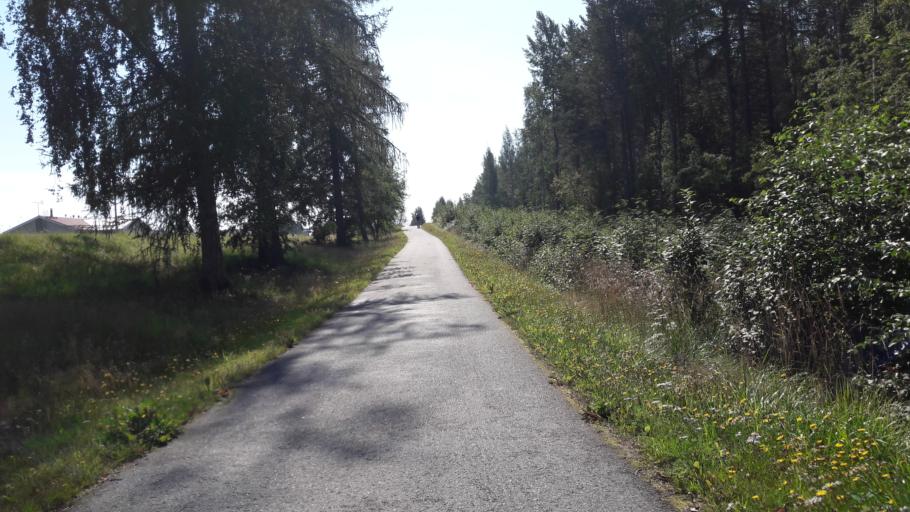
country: FI
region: North Karelia
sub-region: Joensuu
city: Joensuu
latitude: 62.5589
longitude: 29.8175
